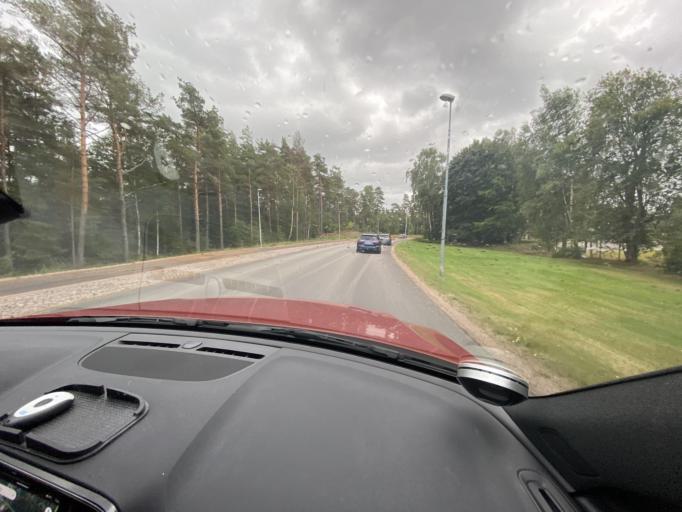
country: SE
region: Kronoberg
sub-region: Markaryds Kommun
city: Markaryd
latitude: 56.4574
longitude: 13.6184
